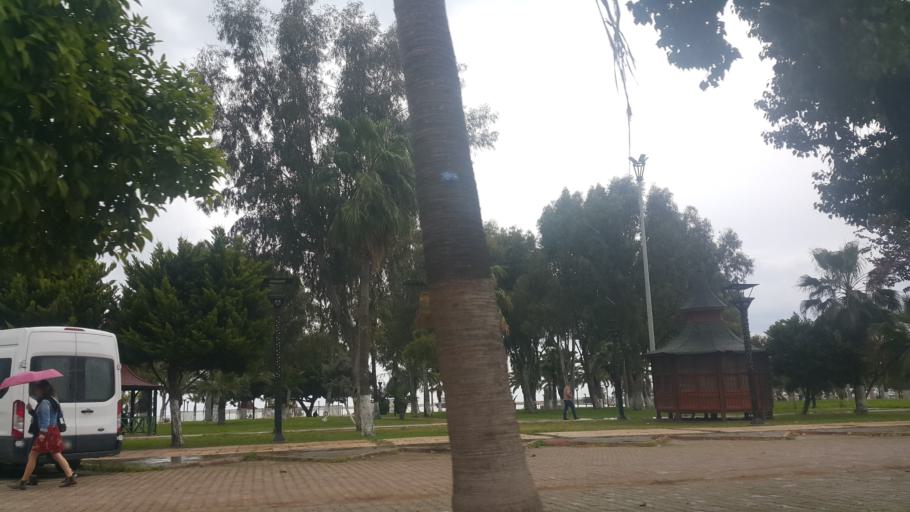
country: TR
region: Mersin
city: Mercin
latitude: 36.7937
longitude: 34.6267
